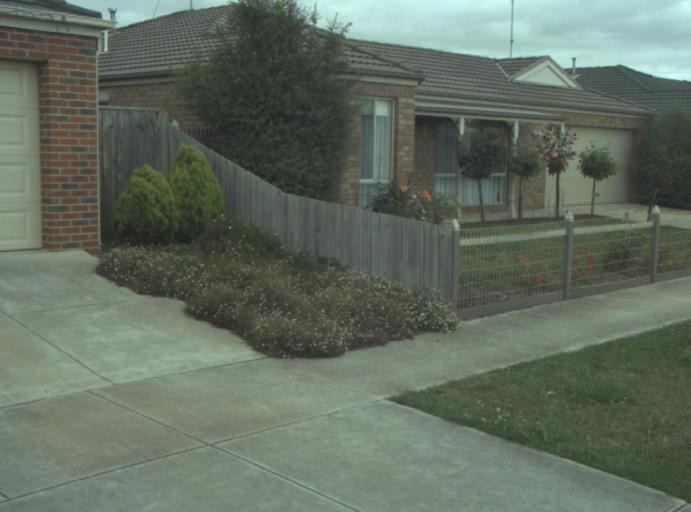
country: AU
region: Victoria
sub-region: Greater Geelong
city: Breakwater
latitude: -38.2012
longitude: 144.3507
